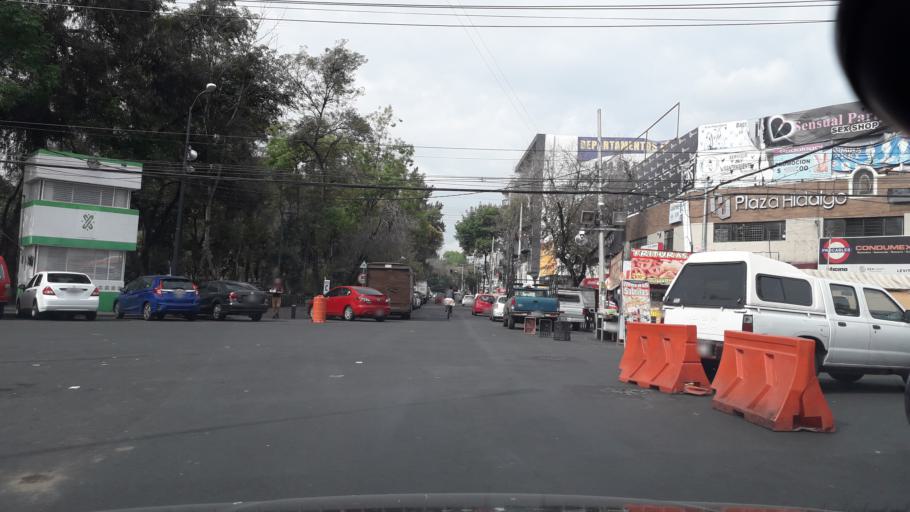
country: MX
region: Mexico City
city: Benito Juarez
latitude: 19.4139
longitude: -99.1468
